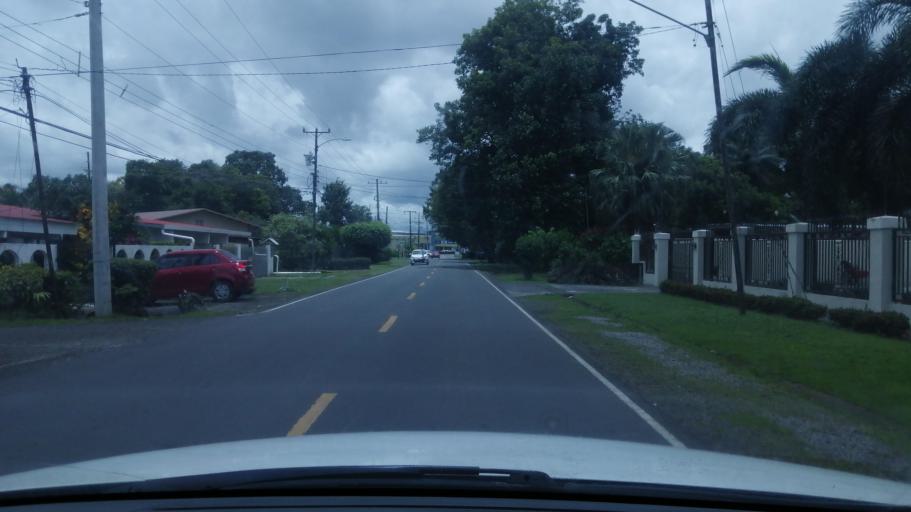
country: PA
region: Chiriqui
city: David
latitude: 8.4413
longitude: -82.4305
